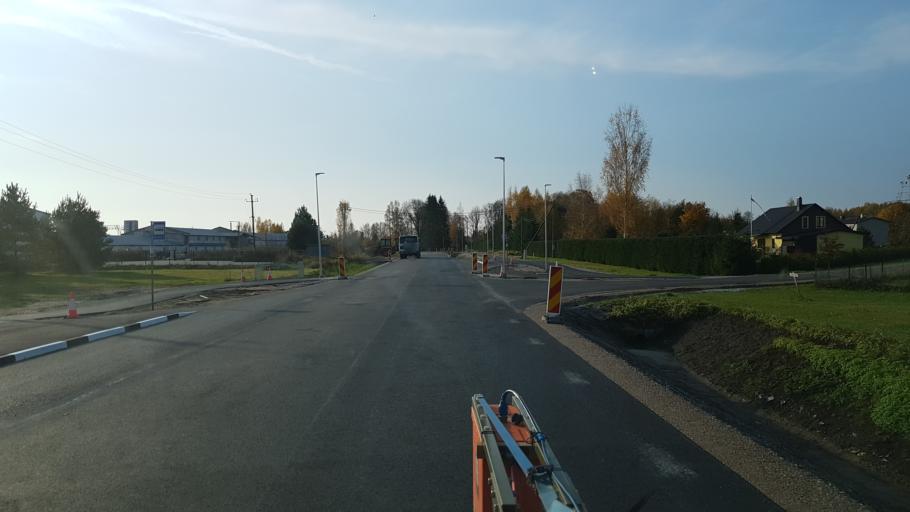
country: EE
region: Paernumaa
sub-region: Paikuse vald
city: Paikuse
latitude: 58.3446
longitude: 24.6208
